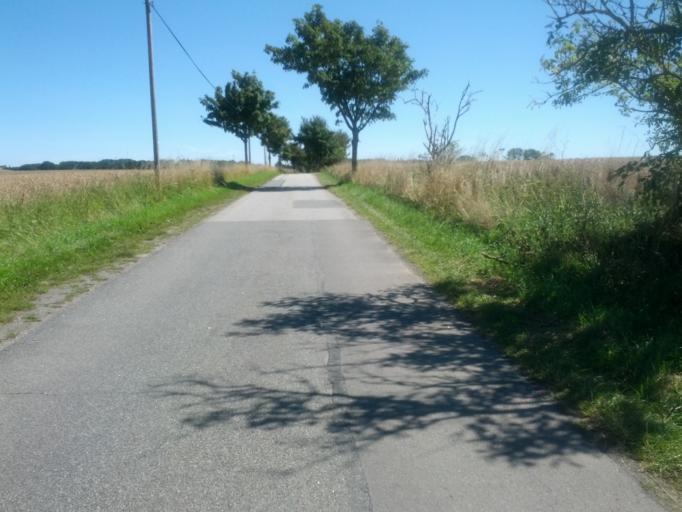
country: DE
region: Mecklenburg-Vorpommern
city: Bastorf
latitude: 54.1189
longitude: 11.6610
